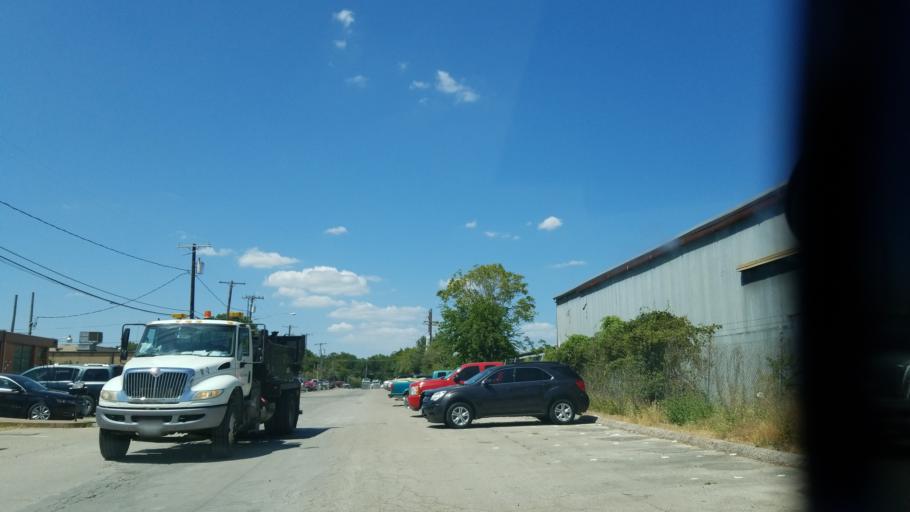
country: US
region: Texas
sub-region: Dallas County
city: Cockrell Hill
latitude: 32.7181
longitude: -96.8857
